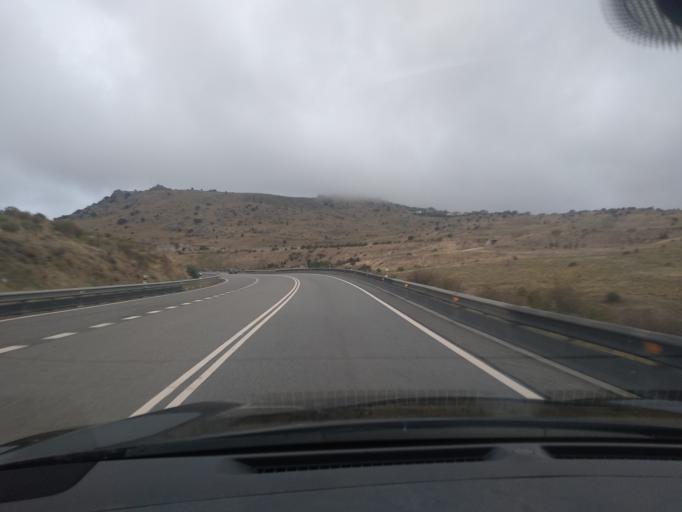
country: ES
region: Castille and Leon
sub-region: Provincia de Segovia
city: Otero de Herreros
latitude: 40.7664
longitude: -4.2045
